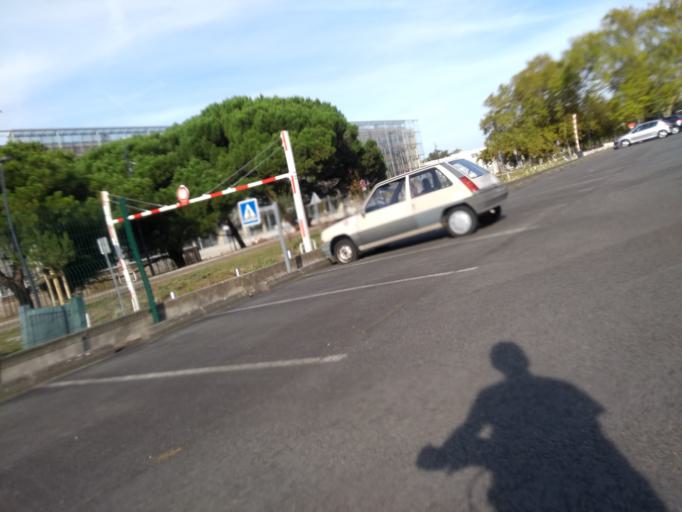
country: FR
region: Aquitaine
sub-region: Departement de la Gironde
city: Talence
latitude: 44.8063
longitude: -0.5997
